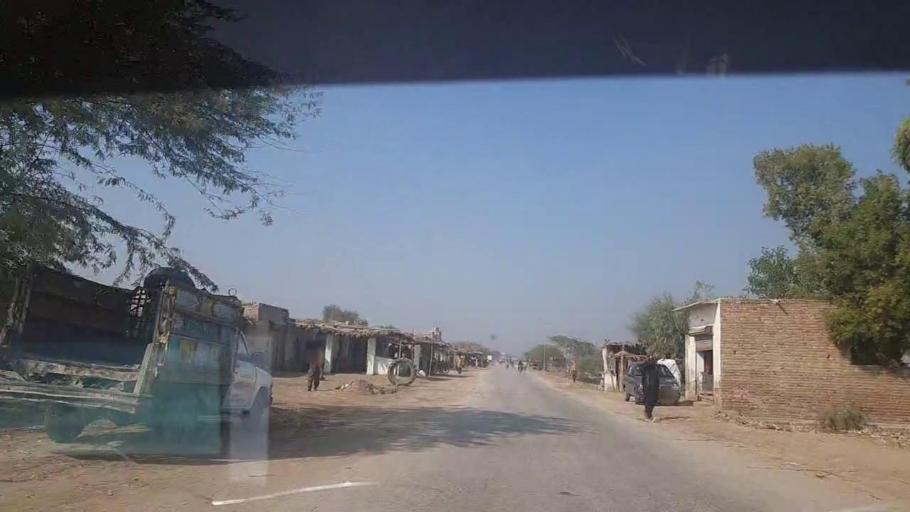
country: PK
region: Sindh
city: Kot Diji
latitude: 27.4131
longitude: 68.6663
